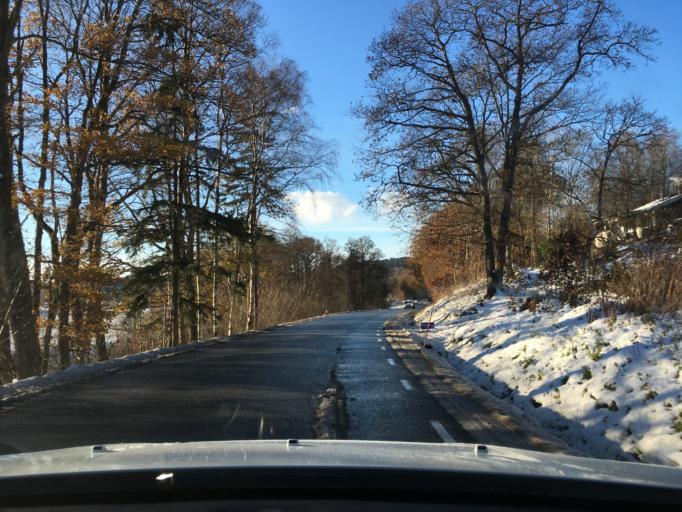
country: SE
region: Vaestra Goetaland
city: Svanesund
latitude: 58.1442
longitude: 11.8012
